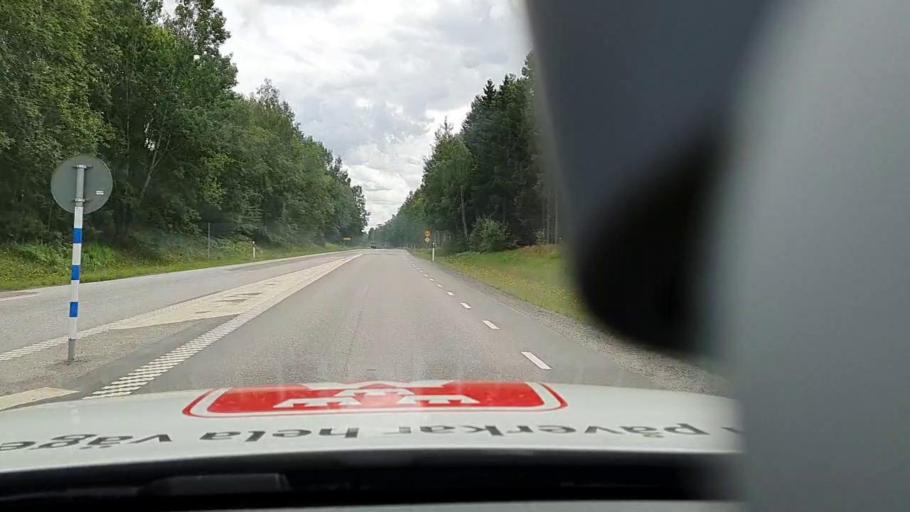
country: SE
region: Vaestra Goetaland
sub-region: Lidkopings Kommun
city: Lidkoping
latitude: 58.5329
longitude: 13.1102
